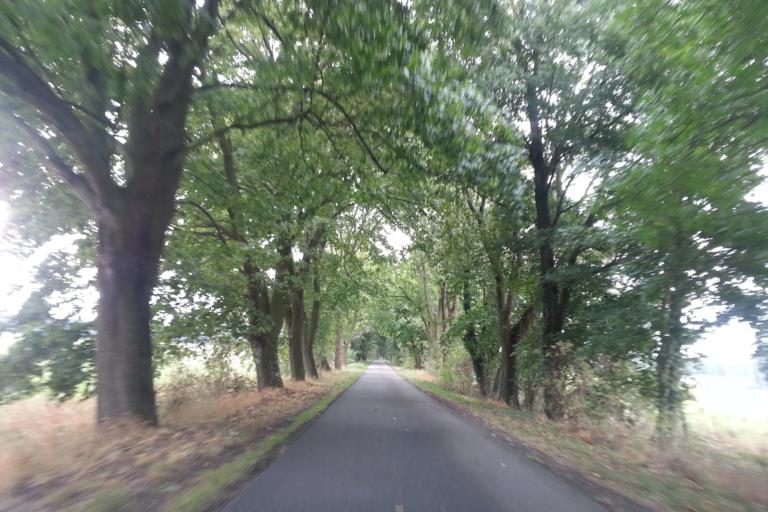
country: DE
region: Mecklenburg-Vorpommern
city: Ferdinandshof
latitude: 53.6656
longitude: 13.8729
